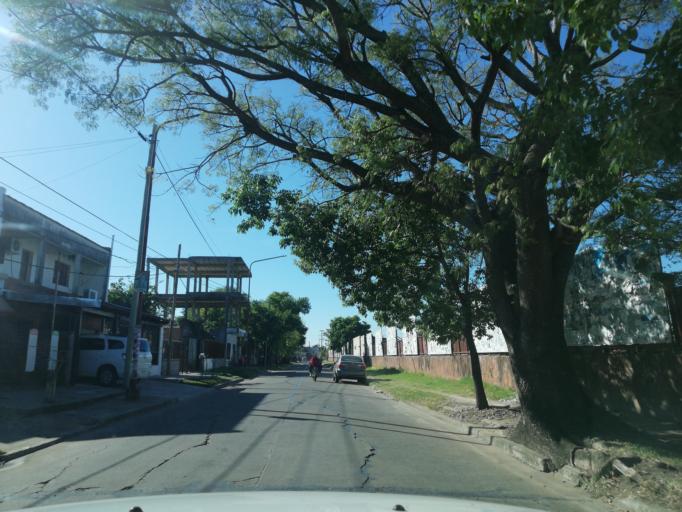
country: AR
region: Corrientes
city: Corrientes
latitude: -27.4753
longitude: -58.8159
